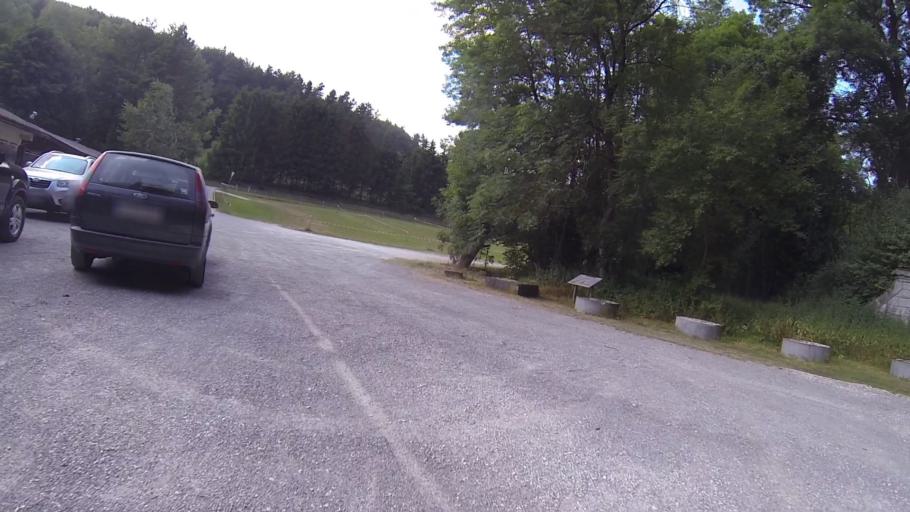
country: DE
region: Baden-Wuerttemberg
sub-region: Tuebingen Region
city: Dornstadt
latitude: 48.4288
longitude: 9.9084
